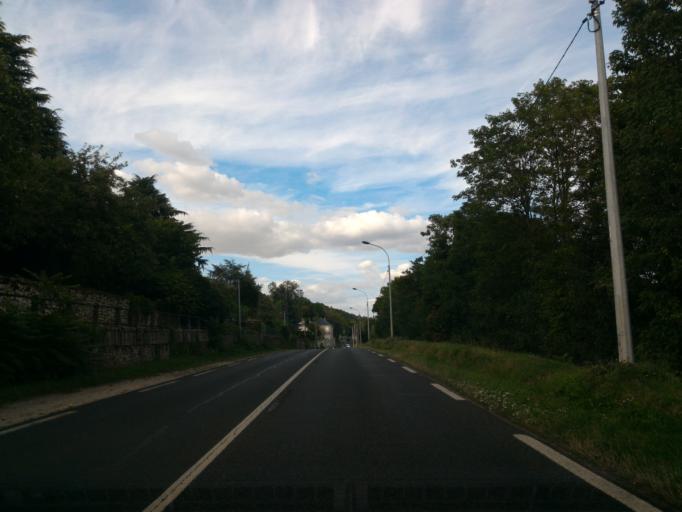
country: FR
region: Centre
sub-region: Departement du Loir-et-Cher
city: Chailles
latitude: 47.5614
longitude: 1.2996
